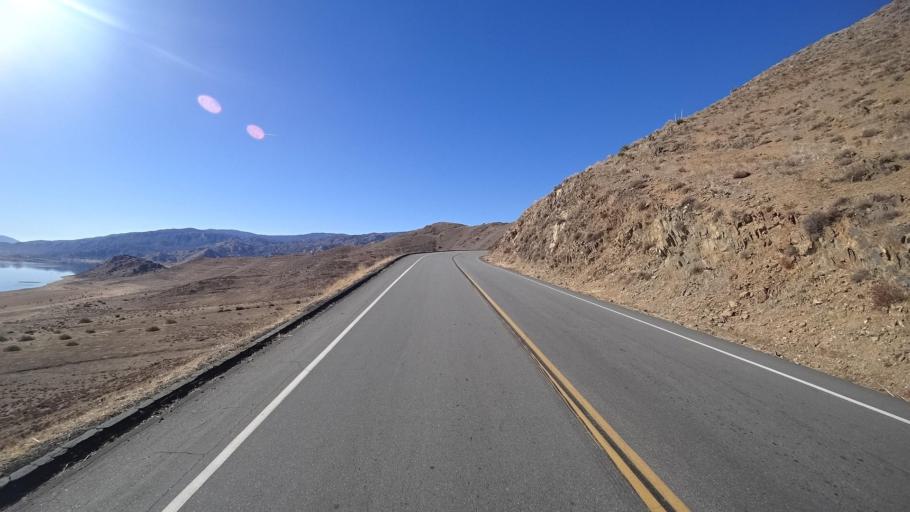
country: US
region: California
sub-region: Kern County
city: Wofford Heights
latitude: 35.6848
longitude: -118.4260
